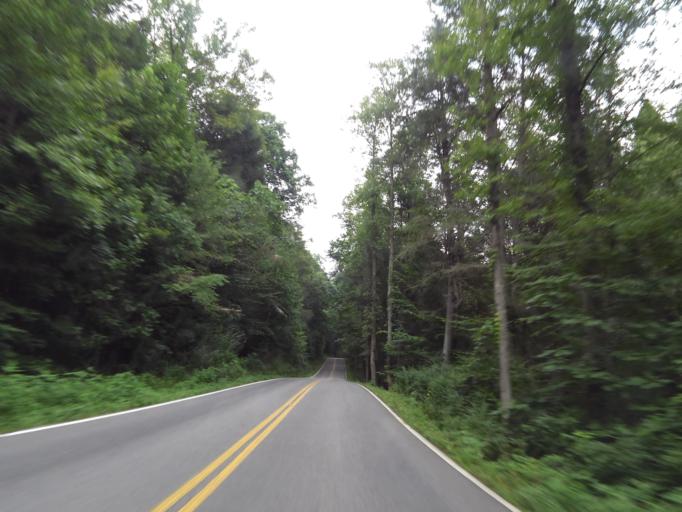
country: US
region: Tennessee
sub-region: Anderson County
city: Clinton
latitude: 36.1372
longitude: -84.2153
